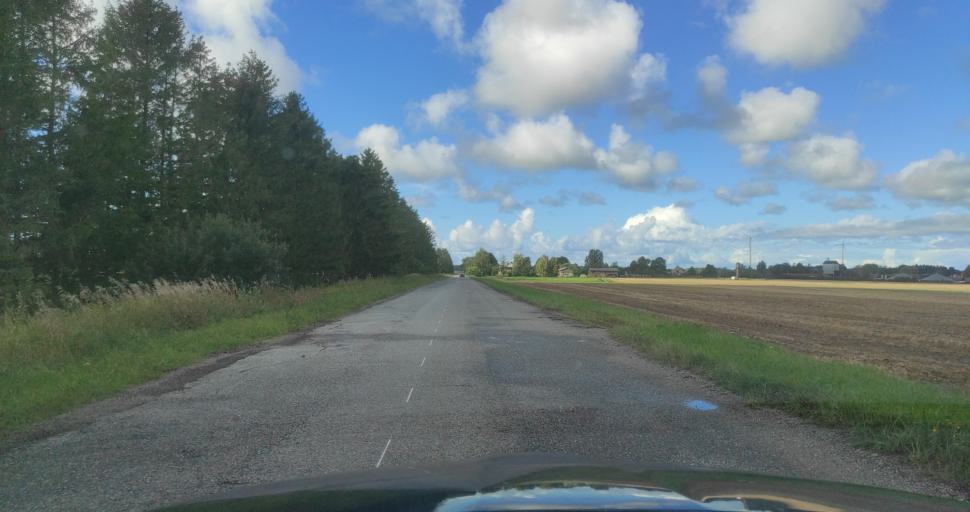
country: LV
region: Ventspils Rajons
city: Piltene
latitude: 57.2632
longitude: 21.5991
